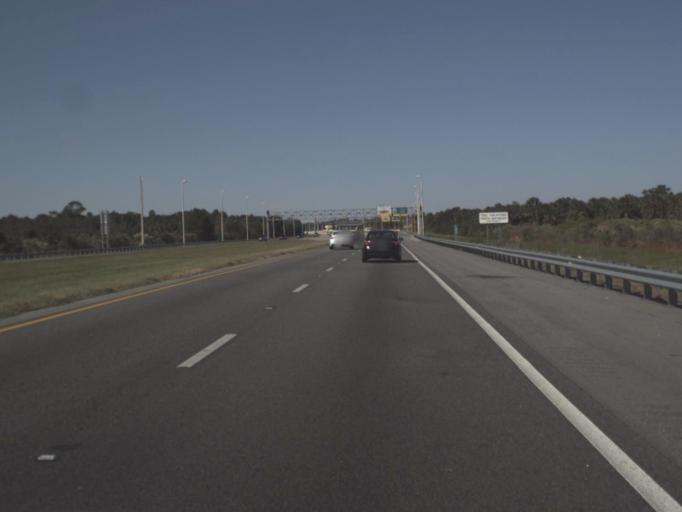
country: US
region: Florida
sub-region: Seminole County
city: Midway
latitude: 28.7320
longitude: -81.2504
